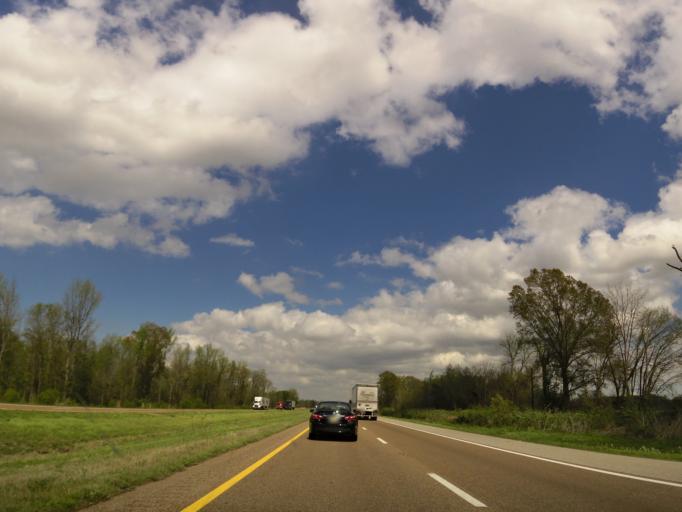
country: US
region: Tennessee
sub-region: Fayette County
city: Hickory Withe
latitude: 35.3077
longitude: -89.5882
